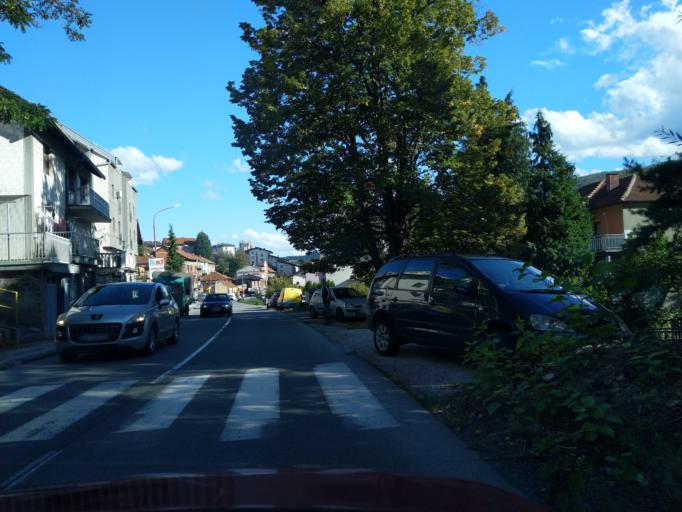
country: RS
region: Central Serbia
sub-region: Zlatiborski Okrug
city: Uzice
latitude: 43.8580
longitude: 19.8316
